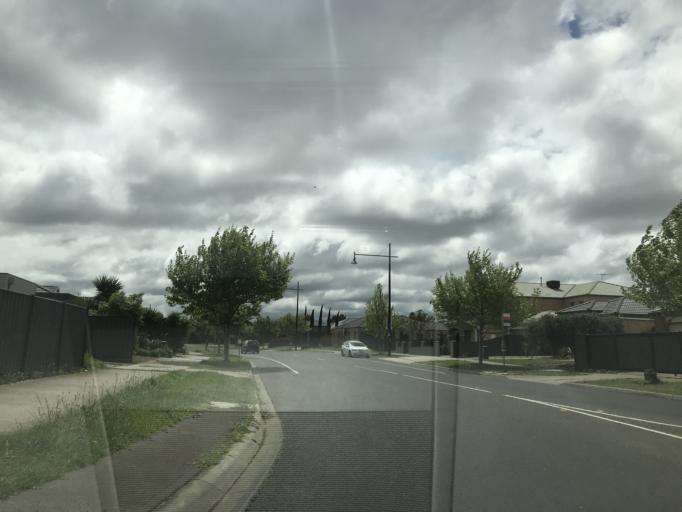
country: AU
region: Victoria
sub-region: Brimbank
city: Derrimut
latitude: -37.7893
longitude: 144.7602
